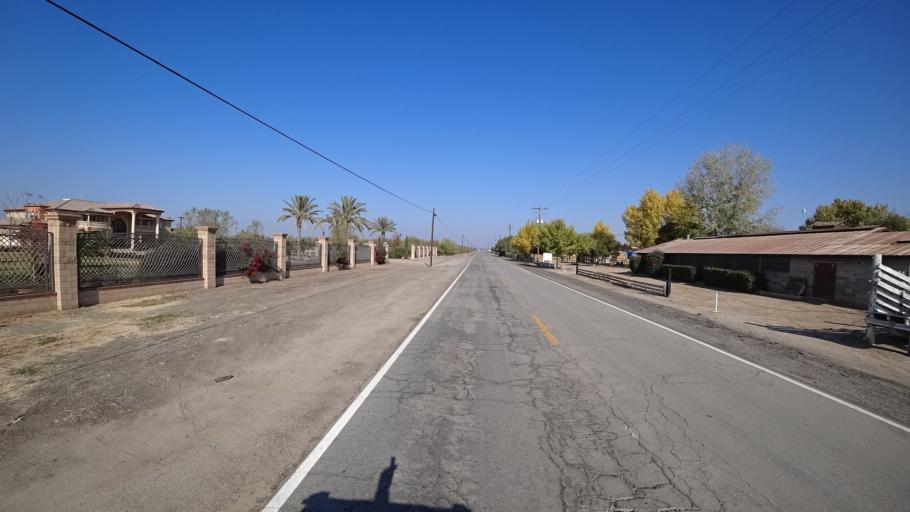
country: US
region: California
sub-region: Kern County
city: Greenfield
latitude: 35.2551
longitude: -119.0390
